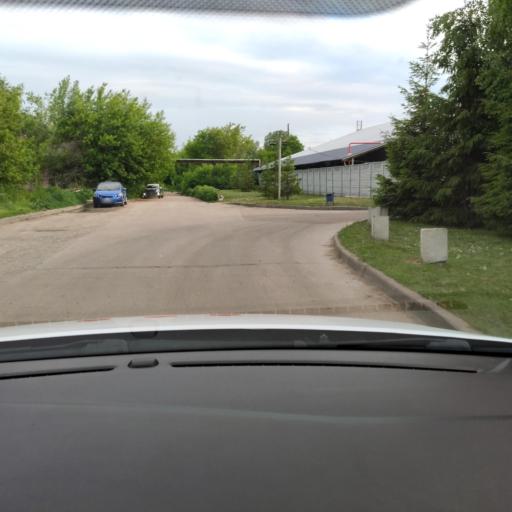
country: RU
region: Tatarstan
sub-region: Gorod Kazan'
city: Kazan
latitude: 55.7409
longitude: 49.1102
